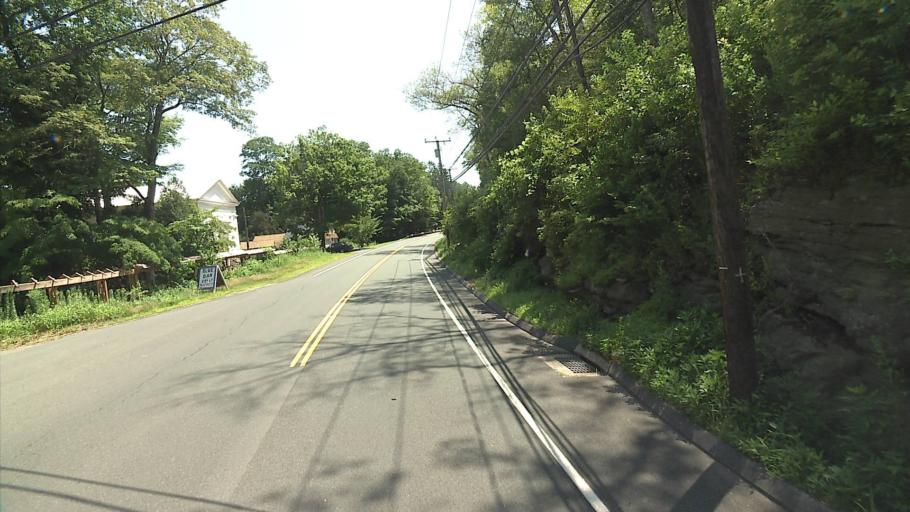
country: US
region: Connecticut
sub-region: Middlesex County
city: East Haddam
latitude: 41.4656
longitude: -72.4803
